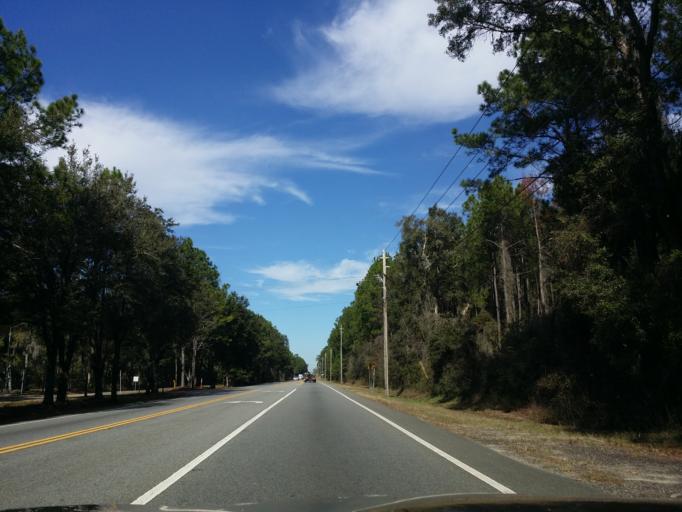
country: US
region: Florida
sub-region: Leon County
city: Woodville
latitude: 30.3601
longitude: -84.2633
